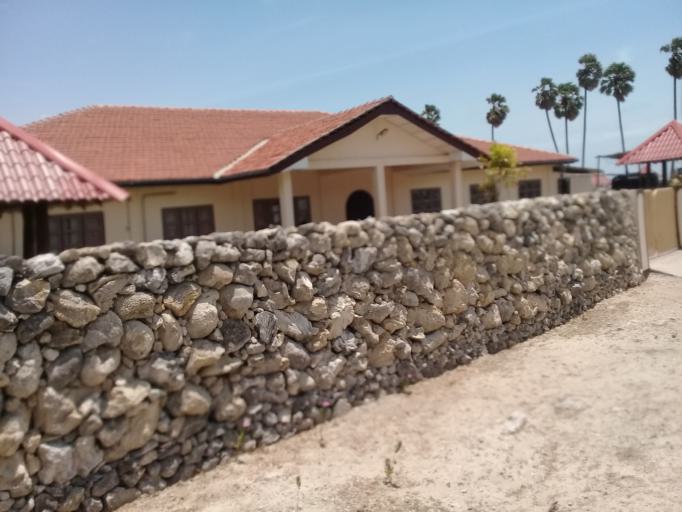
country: LK
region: Northern Province
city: Jaffna
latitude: 9.5275
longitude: 79.7019
